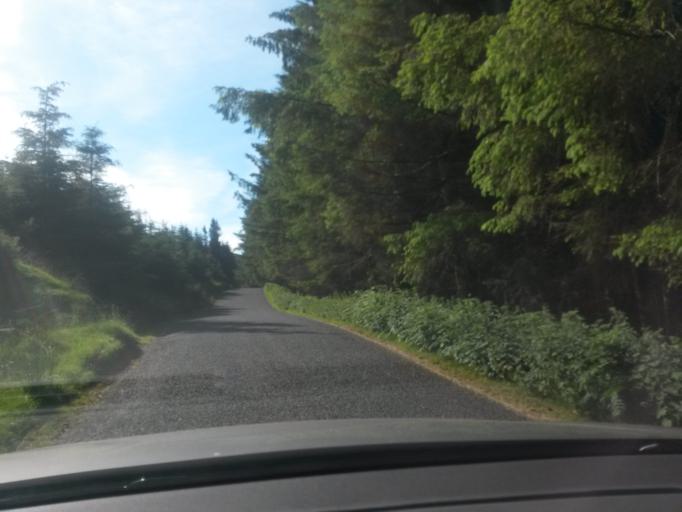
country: IE
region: Leinster
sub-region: Wicklow
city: Enniskerry
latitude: 53.1172
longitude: -6.2670
